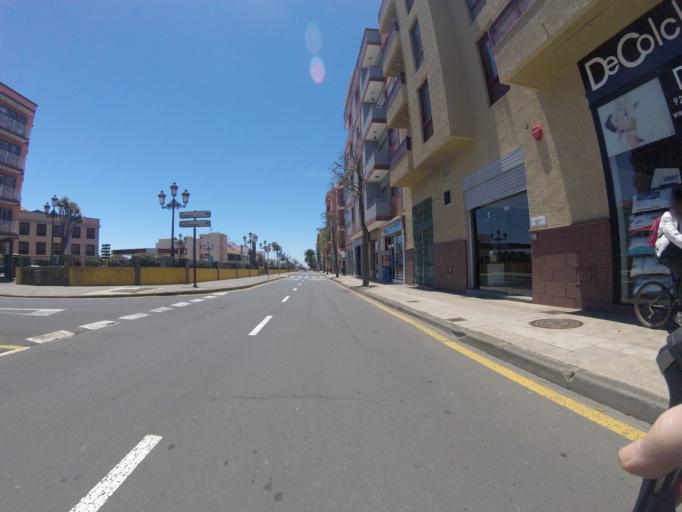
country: ES
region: Canary Islands
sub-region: Provincia de Santa Cruz de Tenerife
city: La Laguna
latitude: 28.4852
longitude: -16.3143
